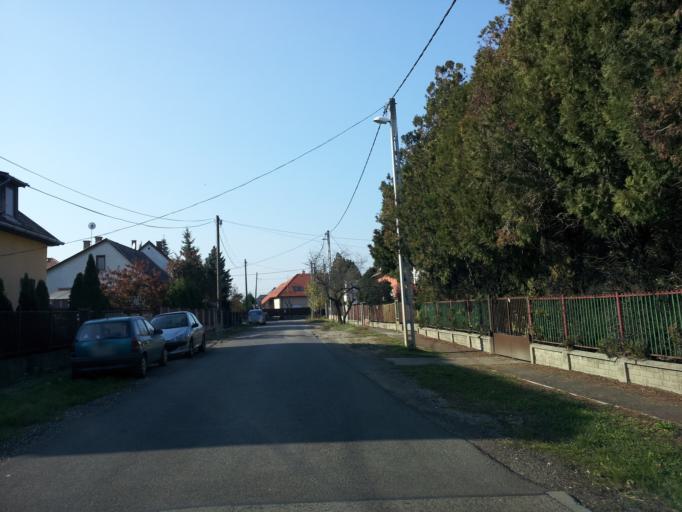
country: HU
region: Budapest
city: Budapest XVIII. keruelet
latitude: 47.4622
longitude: 19.1790
